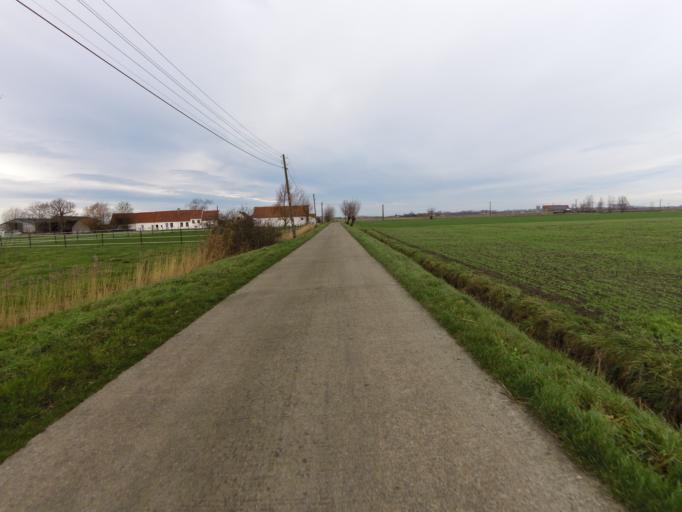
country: BE
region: Flanders
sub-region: Provincie West-Vlaanderen
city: Ostend
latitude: 51.1863
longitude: 2.8833
